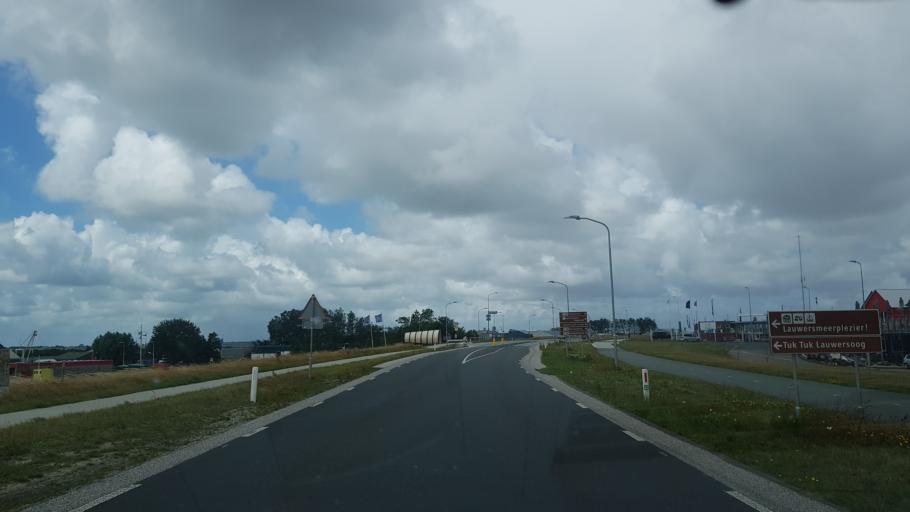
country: NL
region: Friesland
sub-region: Gemeente Dongeradeel
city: Anjum
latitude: 53.4068
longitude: 6.2033
